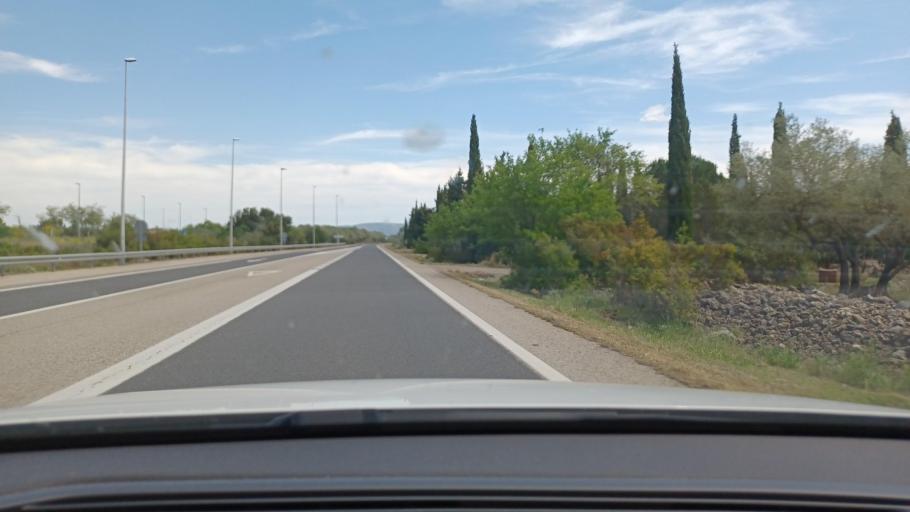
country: ES
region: Catalonia
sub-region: Provincia de Tarragona
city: Mas de Barberans
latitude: 40.6391
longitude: 0.3377
